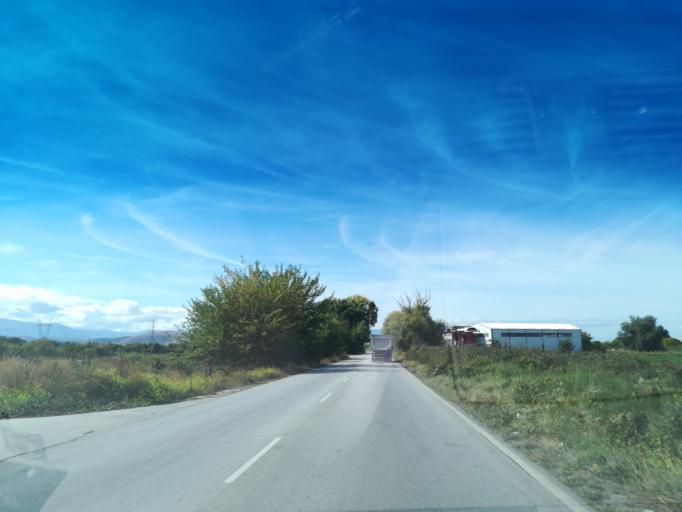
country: BG
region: Plovdiv
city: Stamboliyski
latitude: 42.1177
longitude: 24.5360
